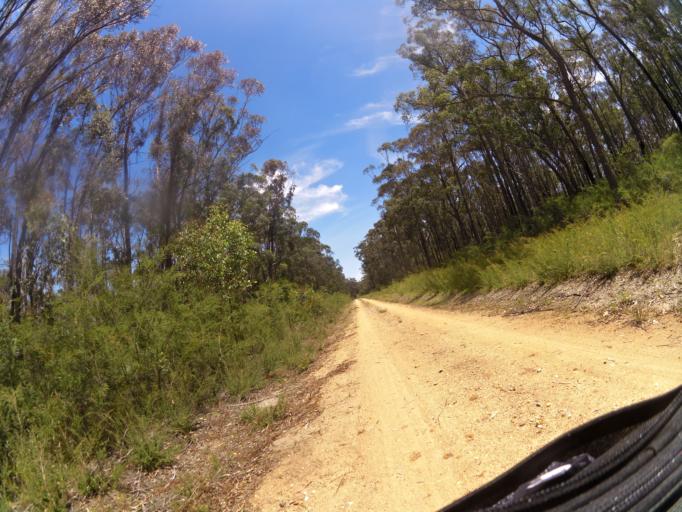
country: AU
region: Victoria
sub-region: East Gippsland
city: Lakes Entrance
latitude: -37.7581
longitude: 147.9584
